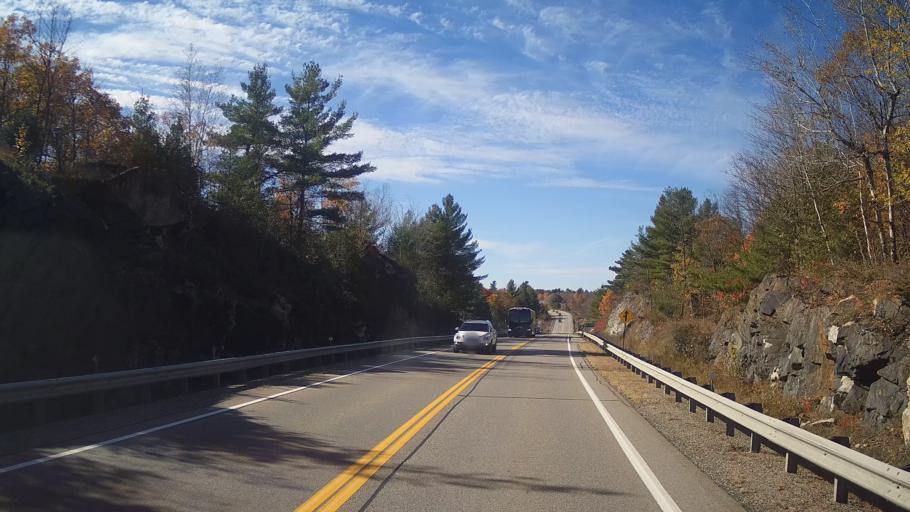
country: CA
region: Ontario
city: Perth
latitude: 44.8038
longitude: -76.6518
